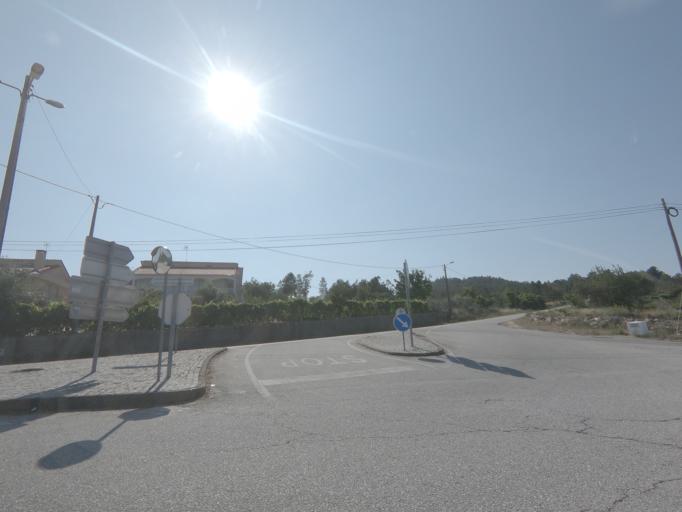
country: PT
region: Viseu
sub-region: Moimenta da Beira
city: Moimenta da Beira
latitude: 40.9984
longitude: -7.5583
